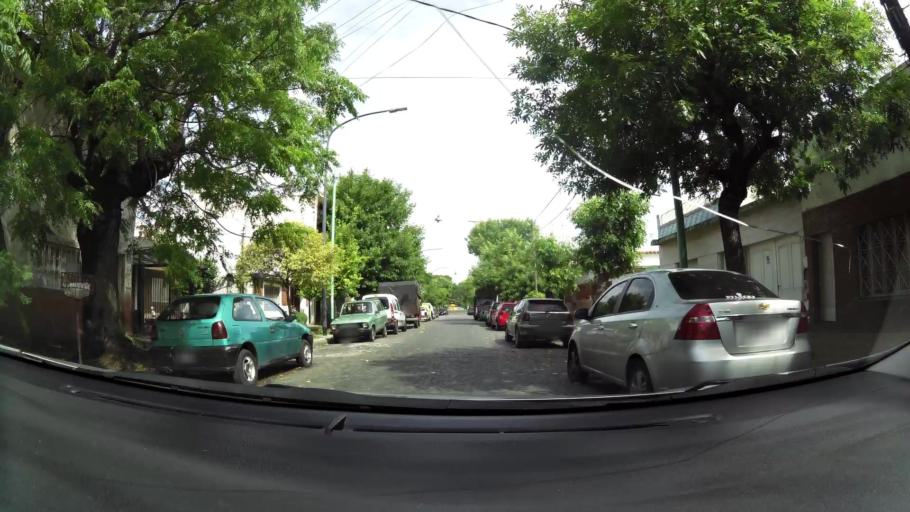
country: AR
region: Buenos Aires F.D.
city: Villa Lugano
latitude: -34.6598
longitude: -58.4324
